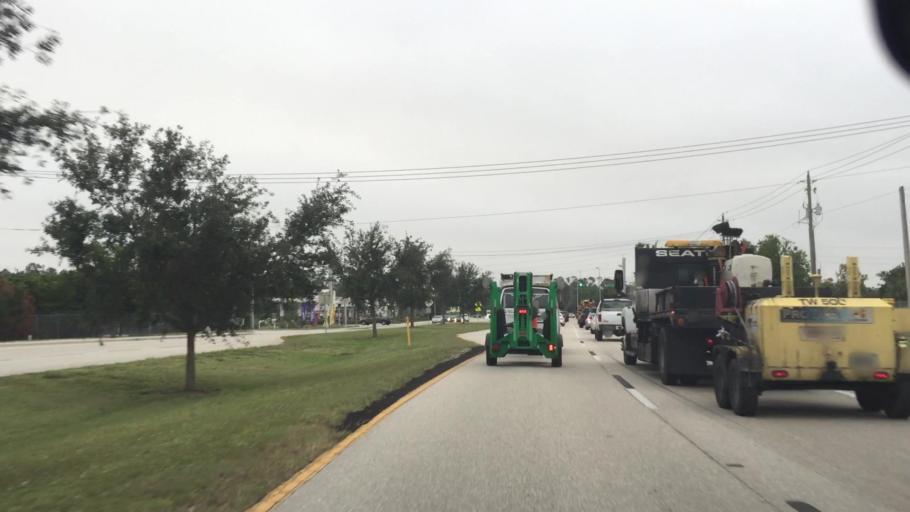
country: US
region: Florida
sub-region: Lee County
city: Three Oaks
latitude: 26.4712
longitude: -81.7940
